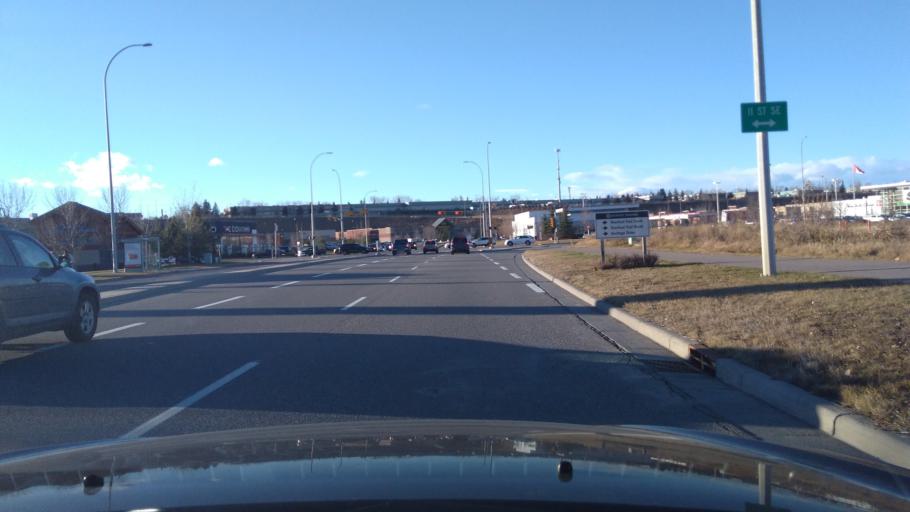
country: CA
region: Alberta
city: Calgary
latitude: 50.9837
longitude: -114.0404
